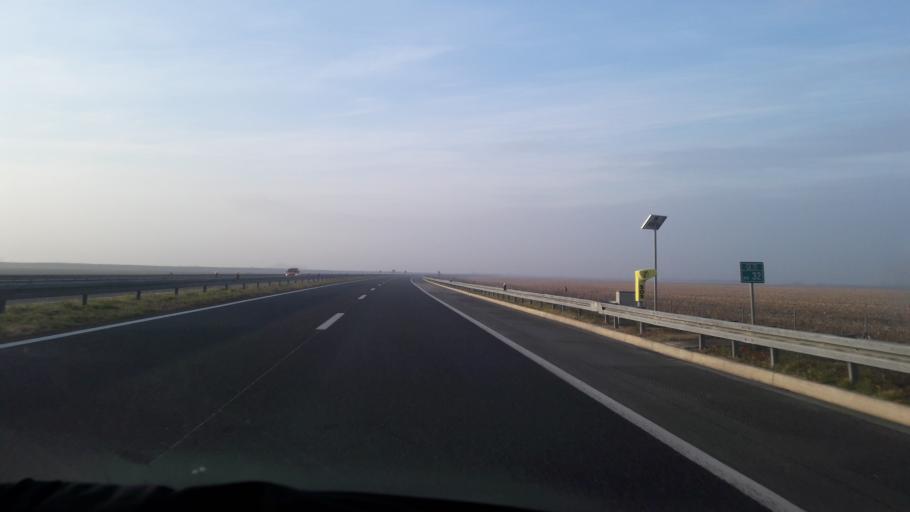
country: HR
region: Osjecko-Baranjska
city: Cepin
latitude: 45.5595
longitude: 18.5445
